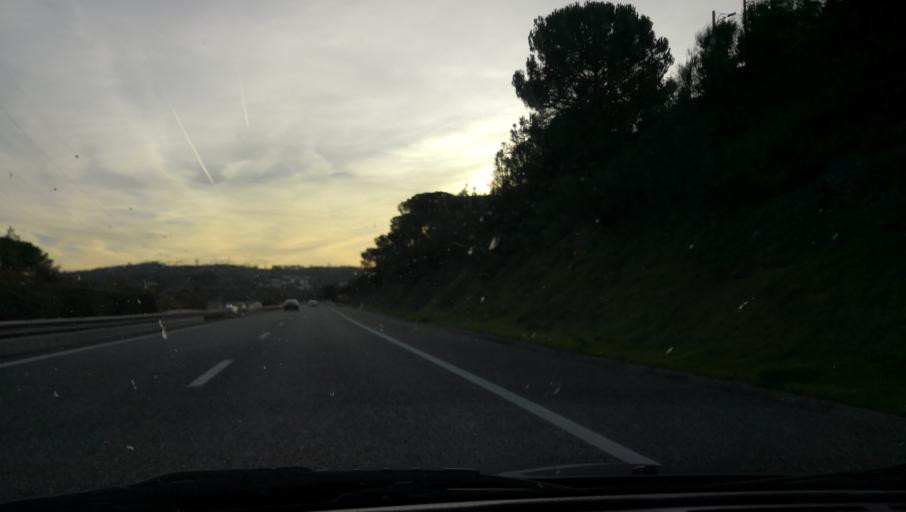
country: PT
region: Coimbra
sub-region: Condeixa-A-Nova
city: Condeixa-a-Nova
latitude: 40.1004
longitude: -8.5308
